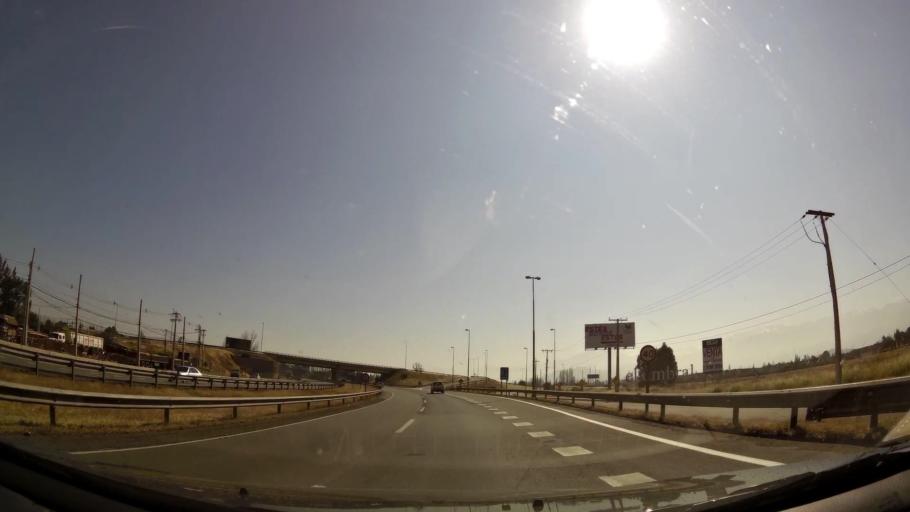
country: CL
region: Santiago Metropolitan
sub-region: Provincia de Chacabuco
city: Chicureo Abajo
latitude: -33.3064
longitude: -70.6994
